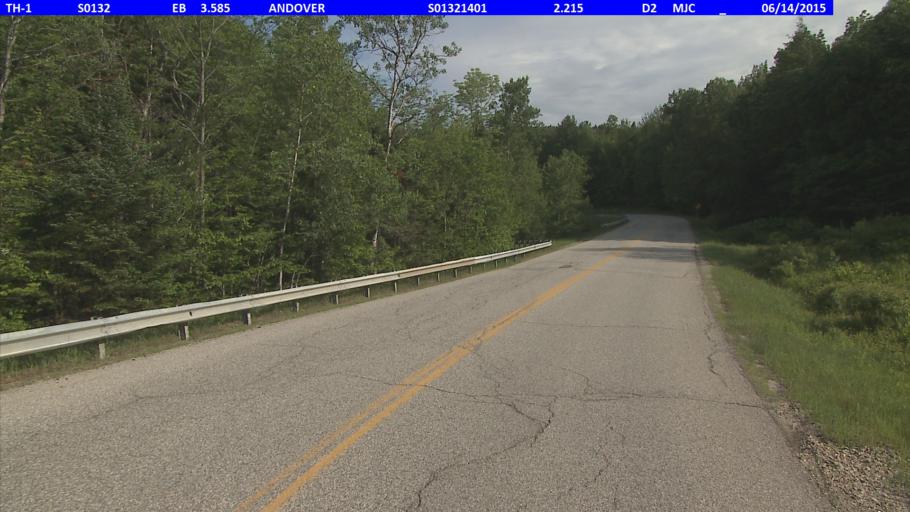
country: US
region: Vermont
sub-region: Windsor County
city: Chester
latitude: 43.2873
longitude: -72.7256
